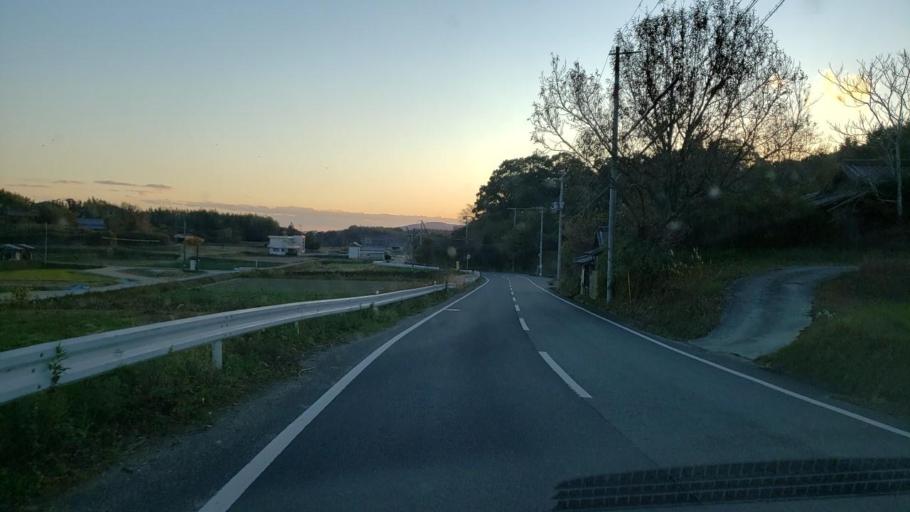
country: JP
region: Hyogo
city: Fukura
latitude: 34.3431
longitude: 134.7823
